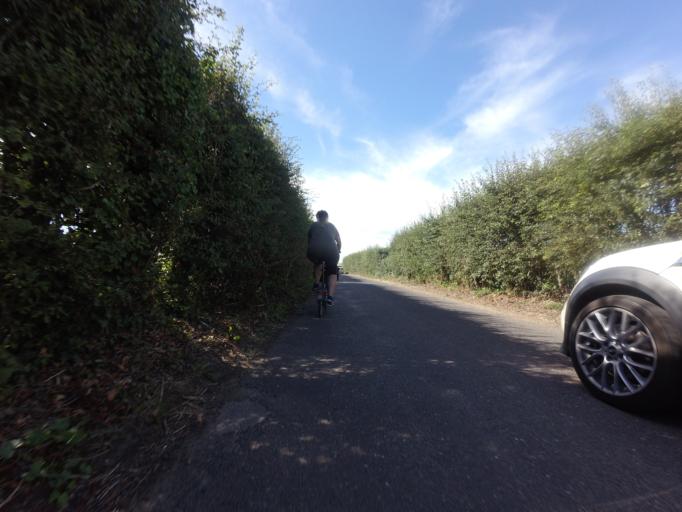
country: GB
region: England
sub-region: Kent
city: Birchington-on-Sea
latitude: 51.3466
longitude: 1.2608
